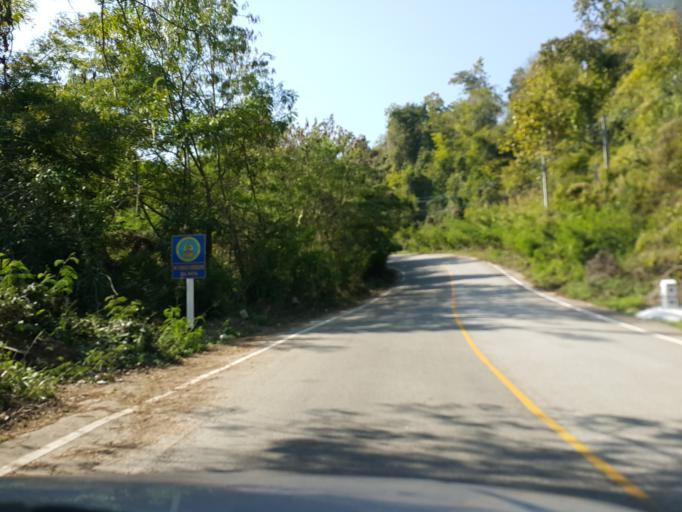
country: TH
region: Chiang Mai
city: Mae Wang
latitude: 18.6187
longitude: 98.7405
